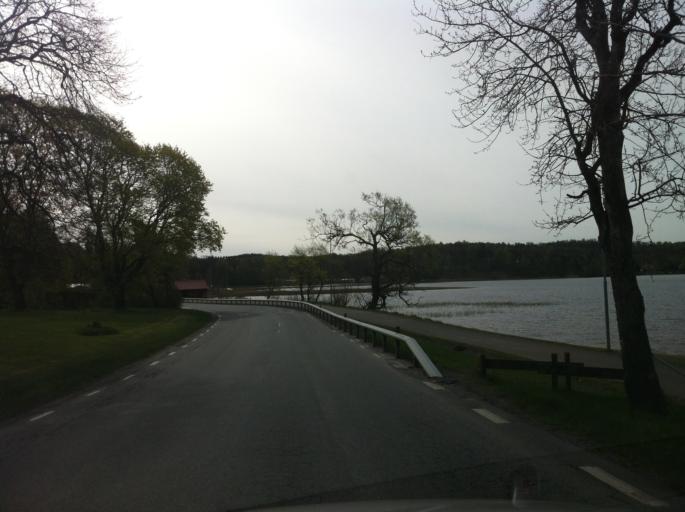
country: SE
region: Vaestra Goetaland
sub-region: Marks Kommun
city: Kinna
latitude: 57.4725
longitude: 12.7071
